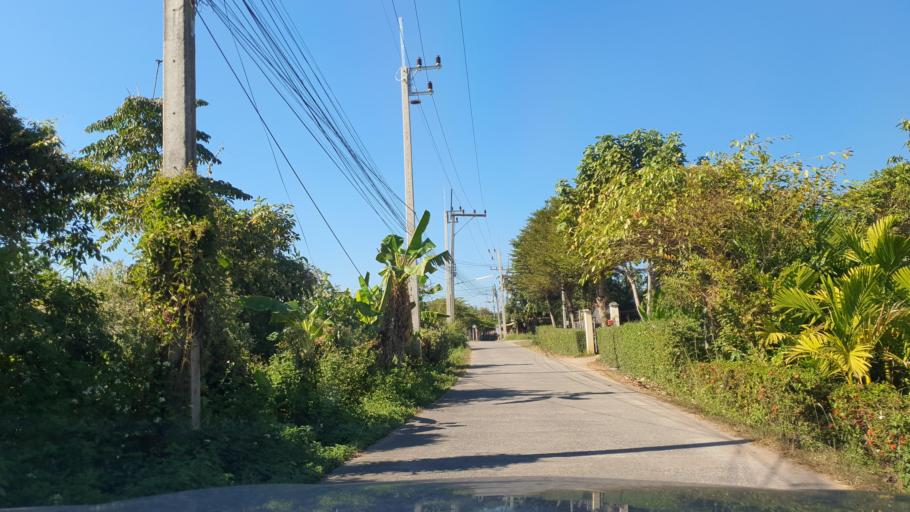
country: TH
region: Chiang Mai
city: San Pa Tong
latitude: 18.6600
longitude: 98.8722
